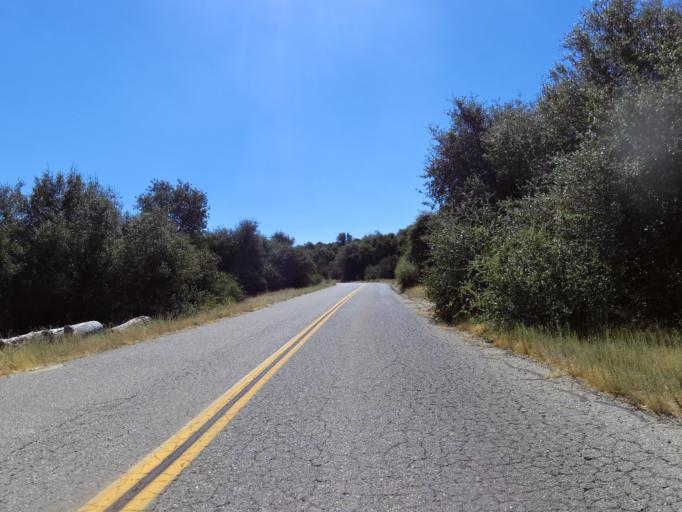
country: US
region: California
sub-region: Madera County
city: Ahwahnee
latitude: 37.3605
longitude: -119.6928
